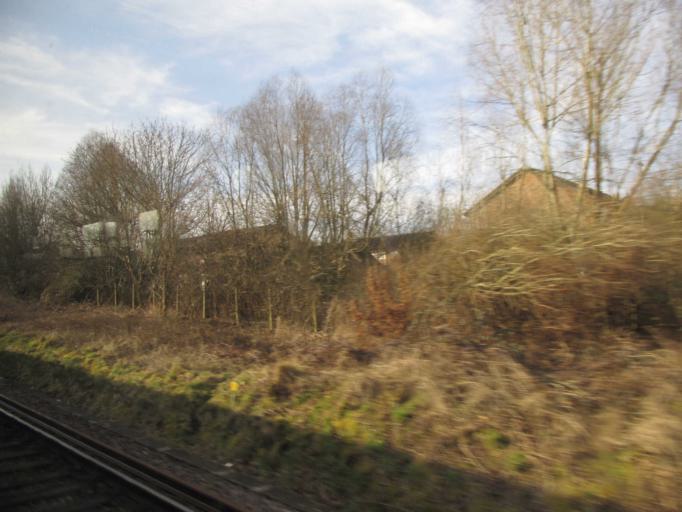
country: GB
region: England
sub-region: Surrey
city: Frimley
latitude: 51.3253
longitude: -0.7706
